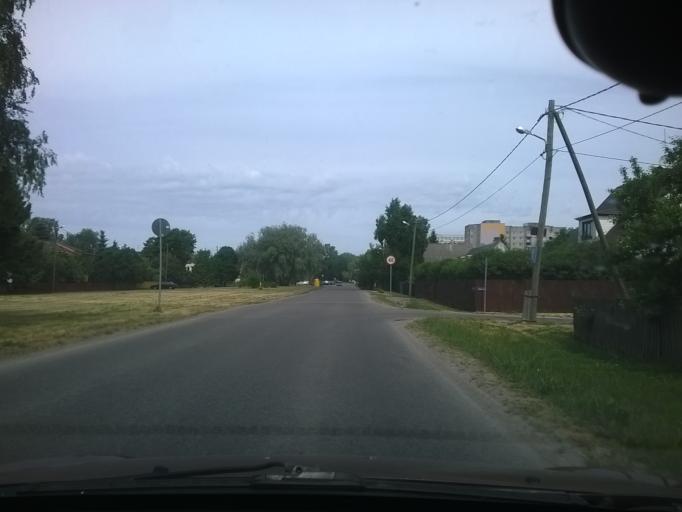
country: EE
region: Harju
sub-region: Tallinna linn
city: Tallinn
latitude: 59.4266
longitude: 24.6899
